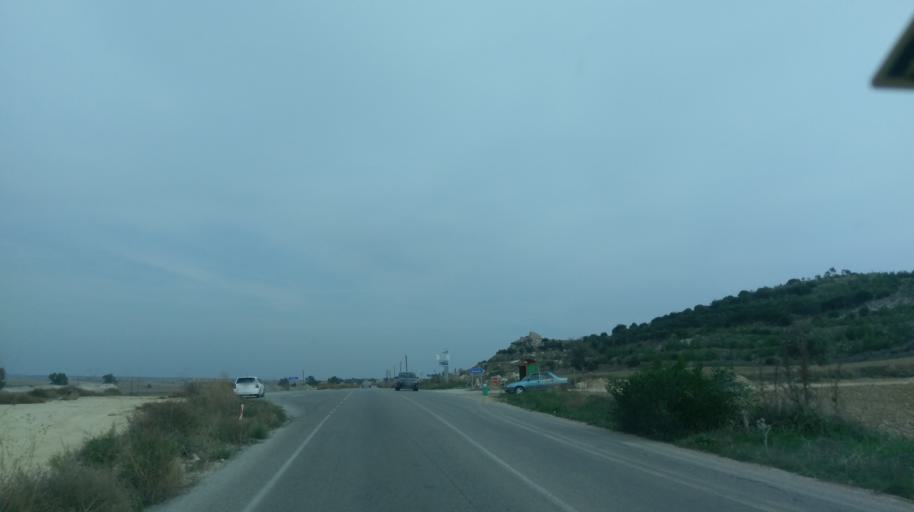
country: CY
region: Ammochostos
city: Trikomo
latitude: 35.3505
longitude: 33.9954
